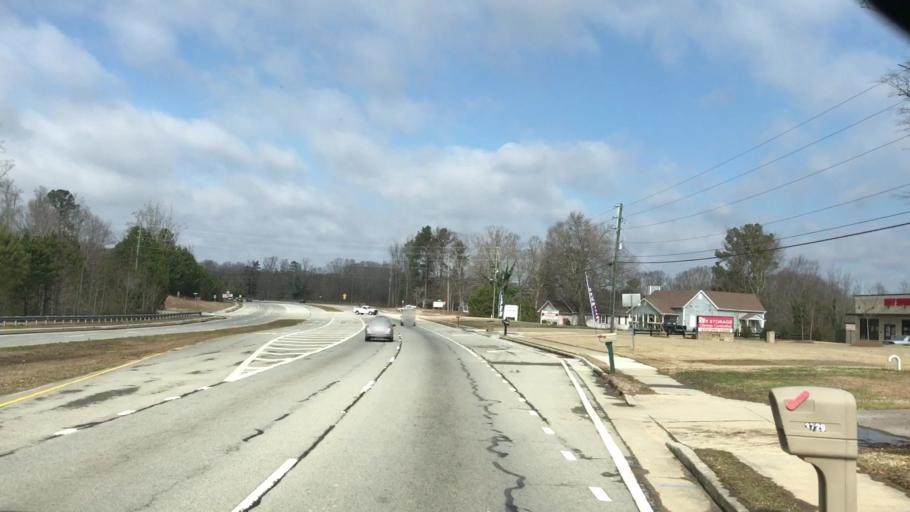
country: US
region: Georgia
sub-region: Hall County
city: Oakwood
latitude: 34.2054
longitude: -83.8561
